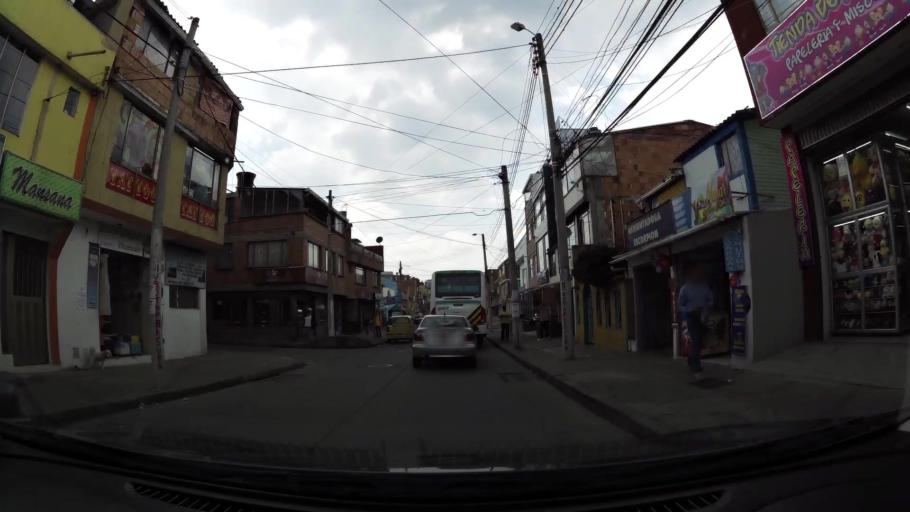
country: CO
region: Cundinamarca
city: La Calera
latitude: 4.7397
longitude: -74.0285
